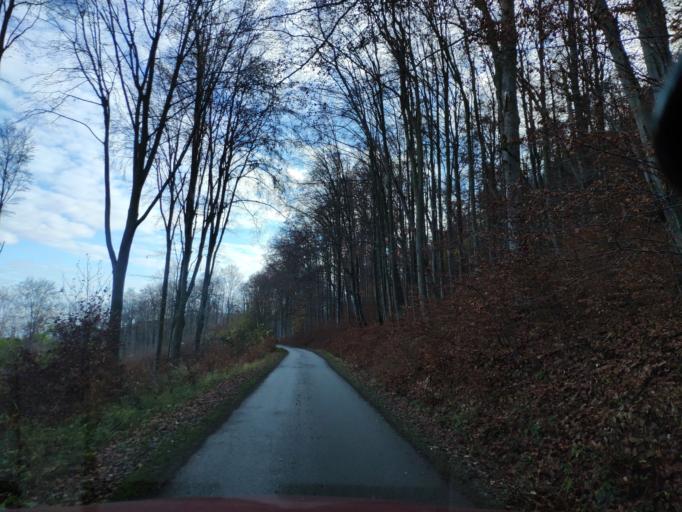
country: HU
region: Borsod-Abauj-Zemplen
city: Gonc
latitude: 48.5853
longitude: 21.4695
